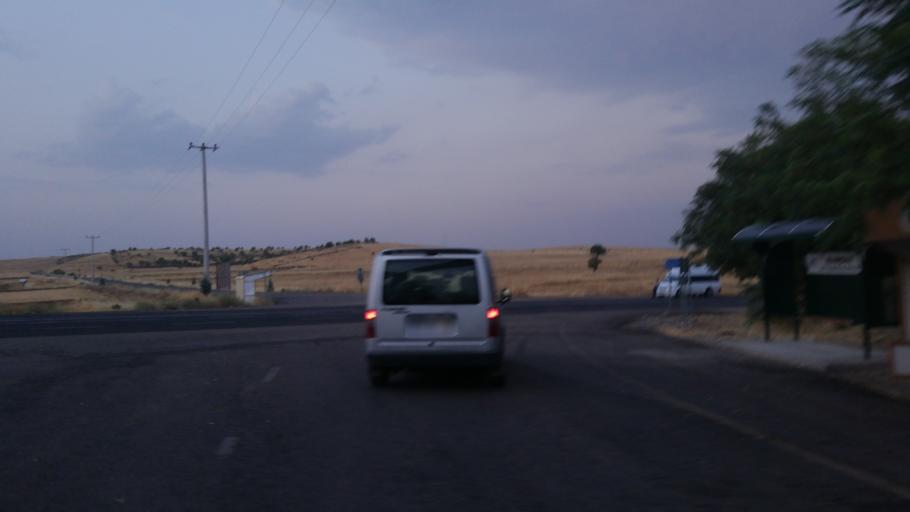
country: TR
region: Mardin
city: Kindirip
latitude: 37.4633
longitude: 41.2263
